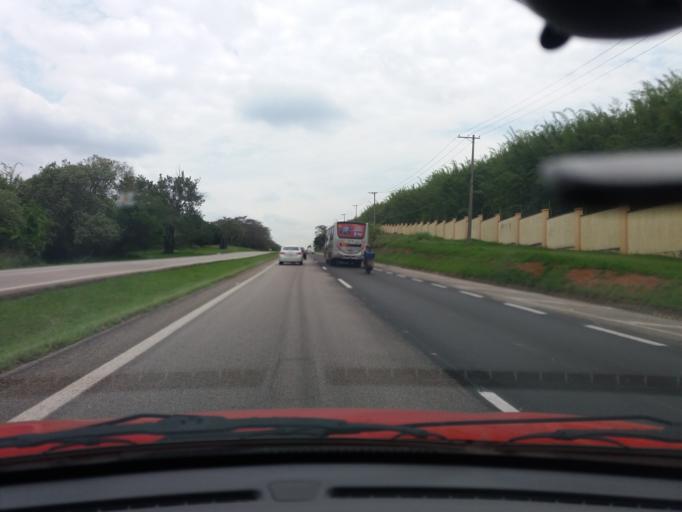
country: BR
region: Sao Paulo
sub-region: Itupeva
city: Itupeva
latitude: -23.2093
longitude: -47.0139
